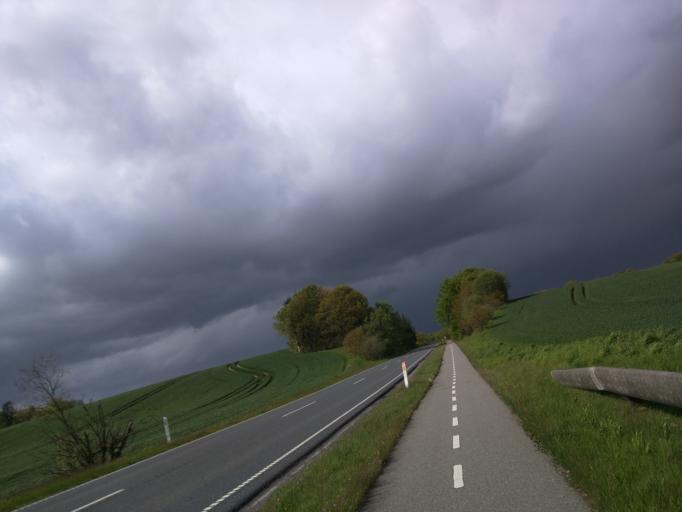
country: DK
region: Central Jutland
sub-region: Silkeborg Kommune
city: Kjellerup
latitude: 56.3155
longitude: 9.4212
